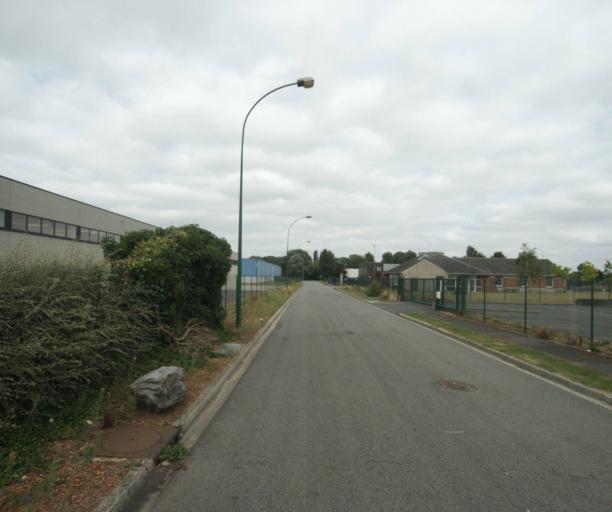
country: FR
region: Nord-Pas-de-Calais
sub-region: Departement du Nord
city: Toufflers
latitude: 50.6679
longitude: 3.2368
